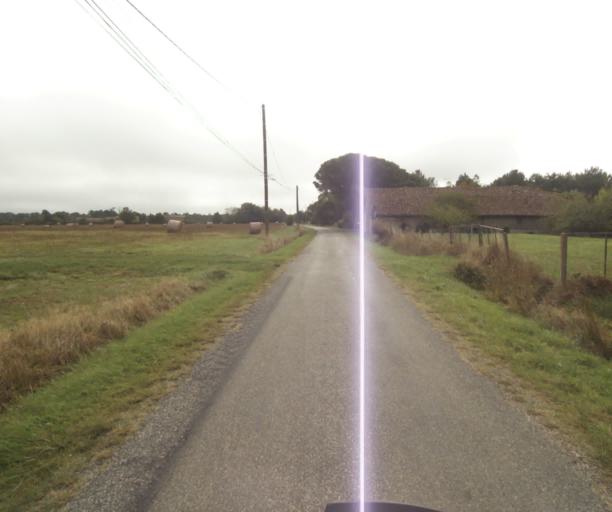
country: FR
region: Midi-Pyrenees
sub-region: Departement du Tarn-et-Garonne
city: Campsas
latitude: 43.8847
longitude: 1.3475
